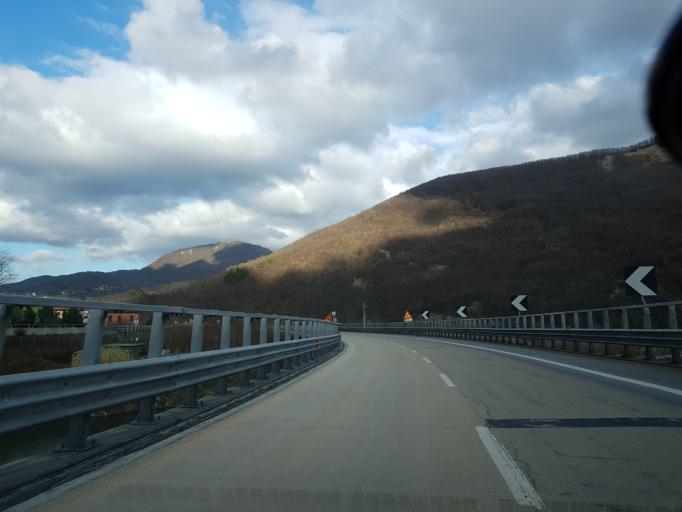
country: IT
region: Liguria
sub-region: Provincia di Genova
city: Borgo Fornari-Pieve
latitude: 44.5945
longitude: 8.9536
